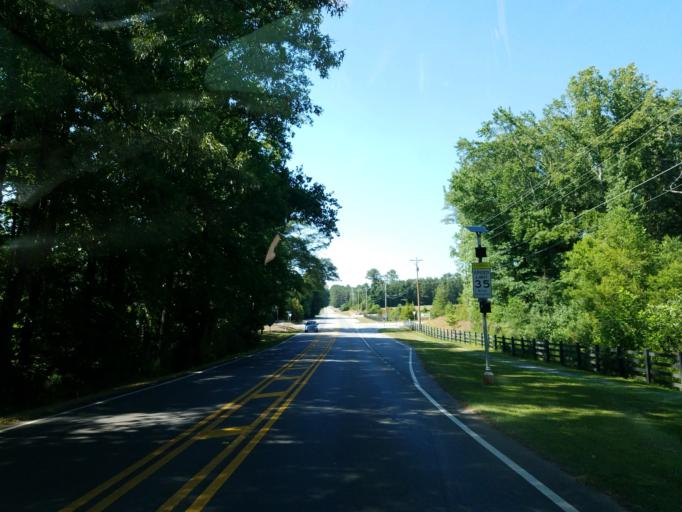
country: US
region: Georgia
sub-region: Fulton County
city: Milton
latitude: 34.1432
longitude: -84.3430
